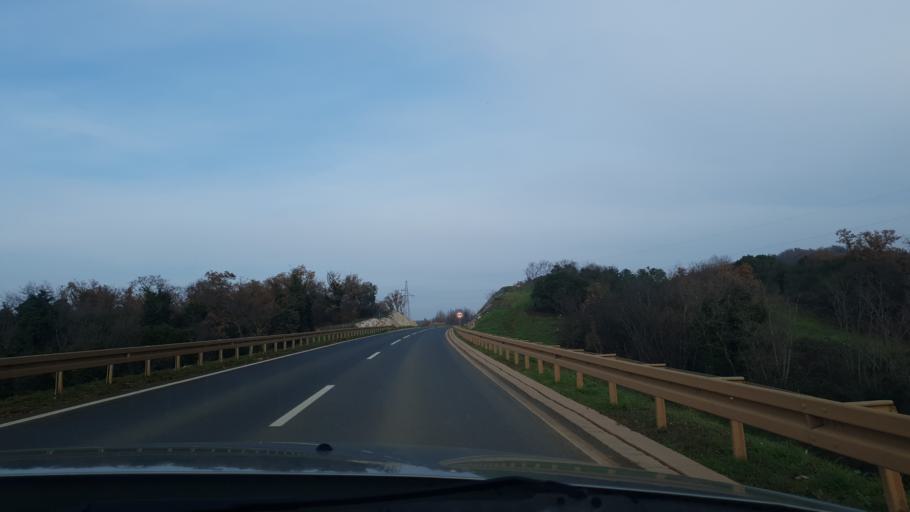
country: HR
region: Istarska
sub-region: Grad Porec
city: Porec
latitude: 45.2152
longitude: 13.6210
